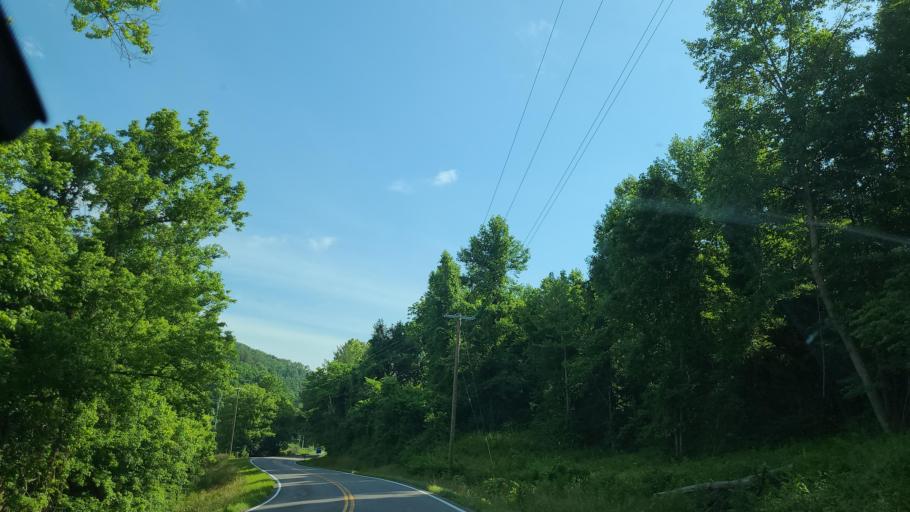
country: US
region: Kentucky
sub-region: Bell County
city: Pineville
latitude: 36.7607
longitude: -83.7803
